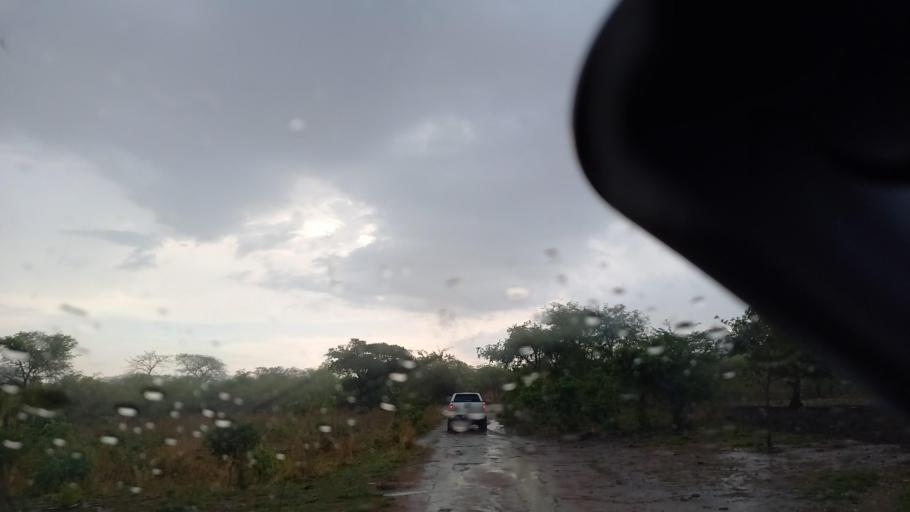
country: ZM
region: Lusaka
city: Kafue
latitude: -15.9453
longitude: 28.2187
